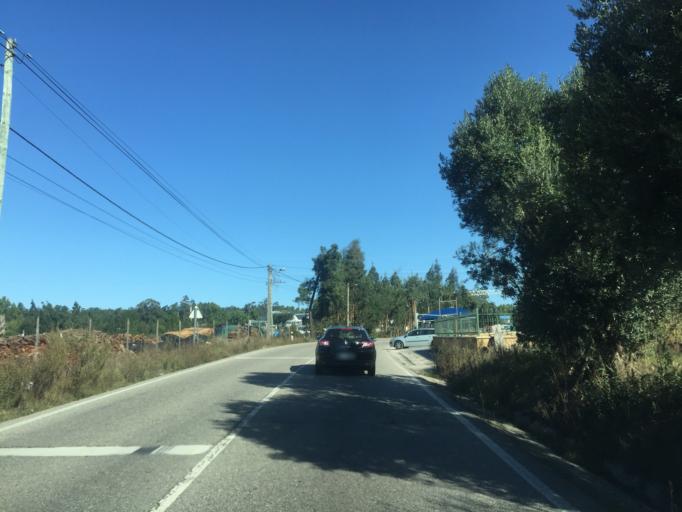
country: PT
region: Leiria
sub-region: Leiria
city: Amor
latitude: 39.8158
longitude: -8.8429
